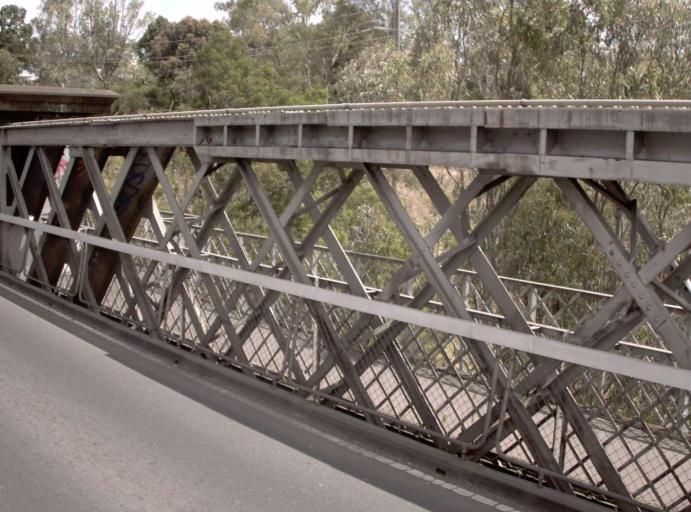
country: AU
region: Victoria
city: Alphington
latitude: -37.7873
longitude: 145.0254
